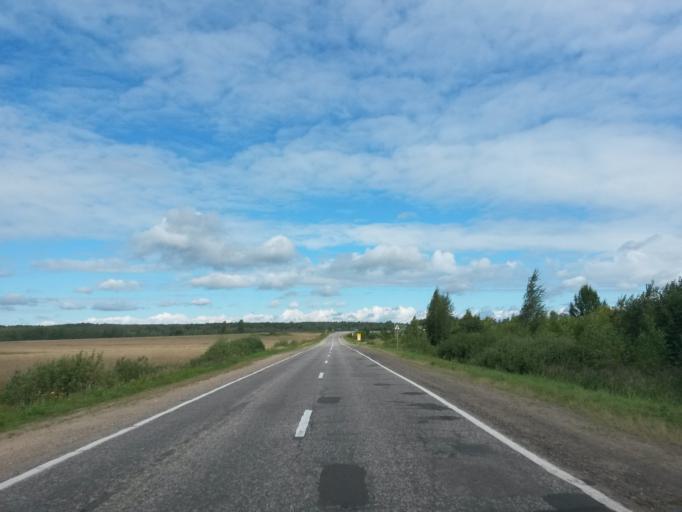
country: RU
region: Jaroslavl
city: Krasnyye Tkachi
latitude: 57.4559
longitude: 39.9110
